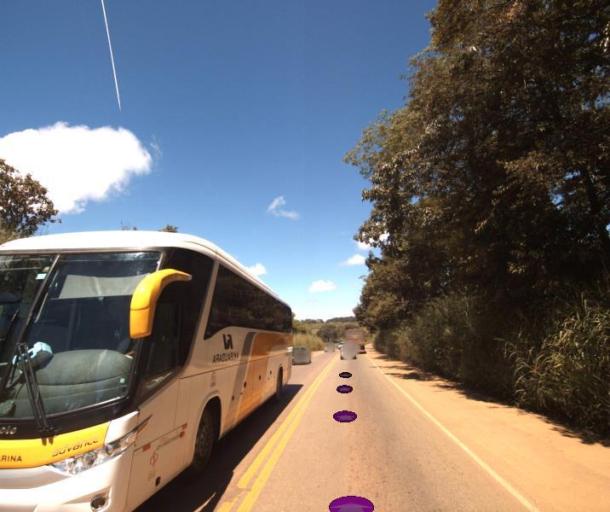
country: BR
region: Goias
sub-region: Anapolis
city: Anapolis
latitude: -16.1138
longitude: -49.0319
